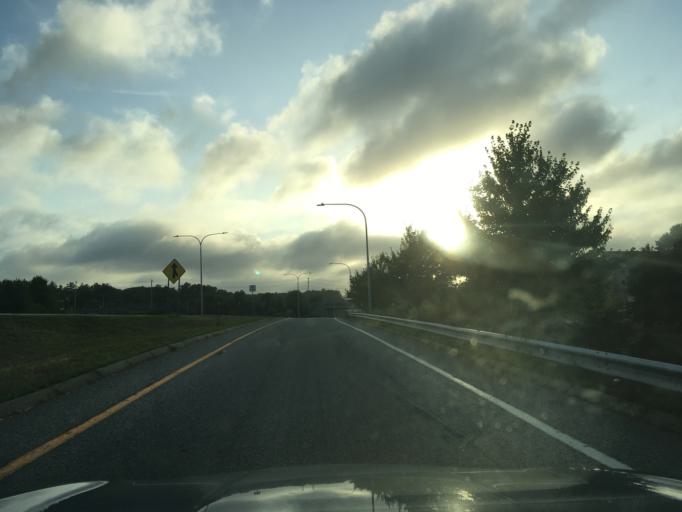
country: US
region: Rhode Island
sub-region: Washington County
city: North Kingstown
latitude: 41.6041
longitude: -71.4508
